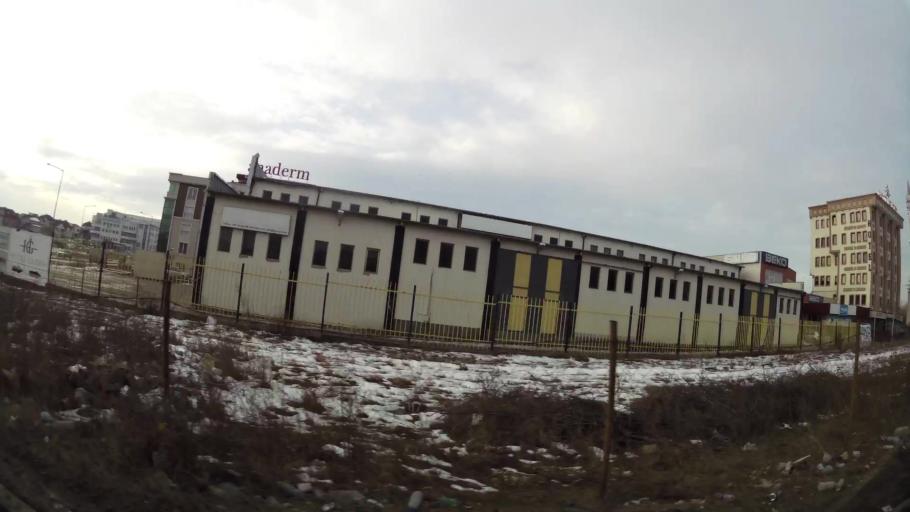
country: XK
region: Pristina
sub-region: Komuna e Prishtines
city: Pristina
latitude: 42.6316
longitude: 21.1494
